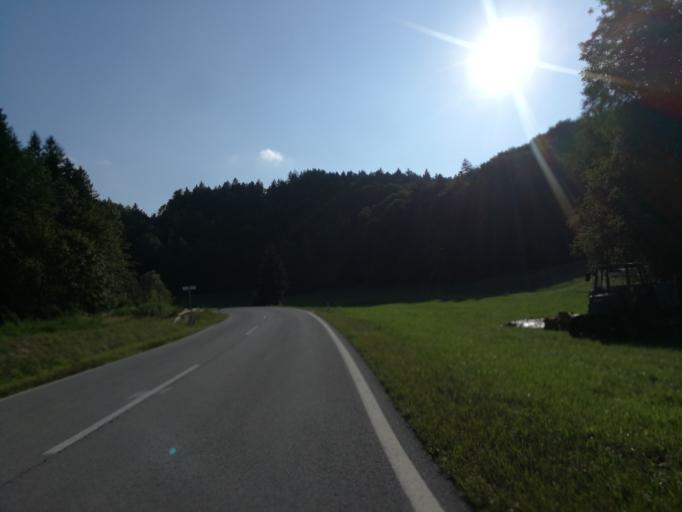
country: AT
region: Salzburg
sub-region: Politischer Bezirk Salzburg-Umgebung
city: Plainfeld
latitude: 47.8446
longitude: 13.1847
